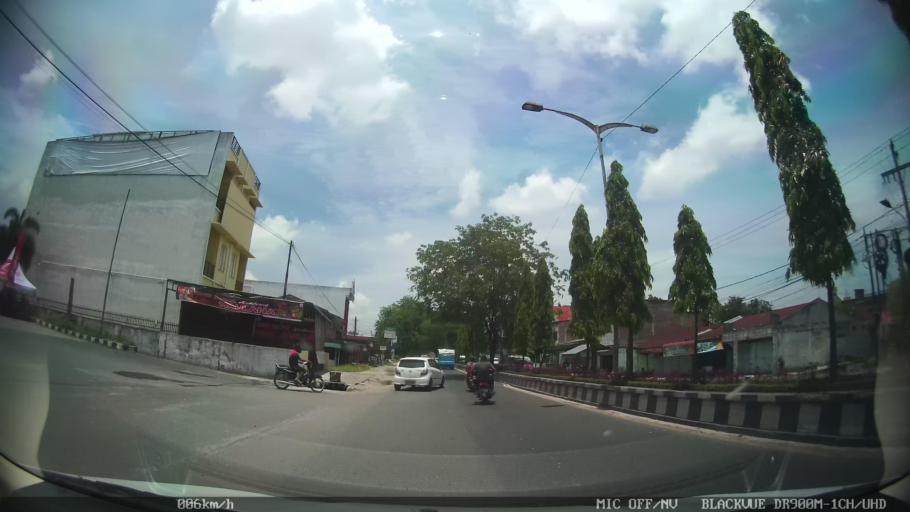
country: ID
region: North Sumatra
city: Percut
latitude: 3.5540
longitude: 98.8736
